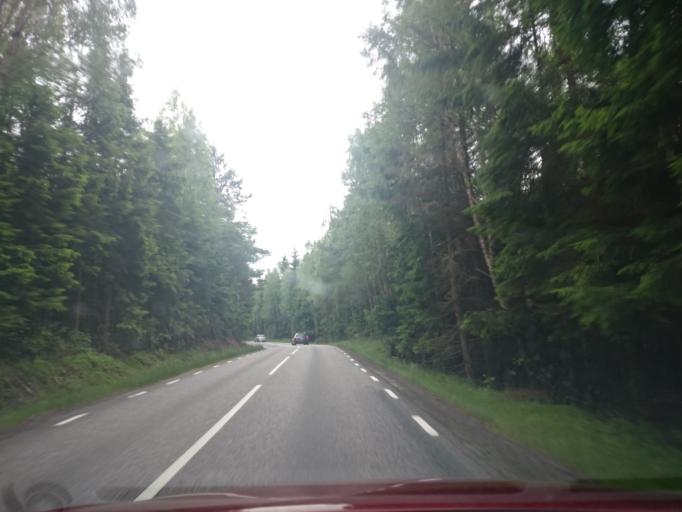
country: SE
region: Vaestra Goetaland
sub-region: Lerums Kommun
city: Stenkullen
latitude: 57.7255
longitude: 12.3462
